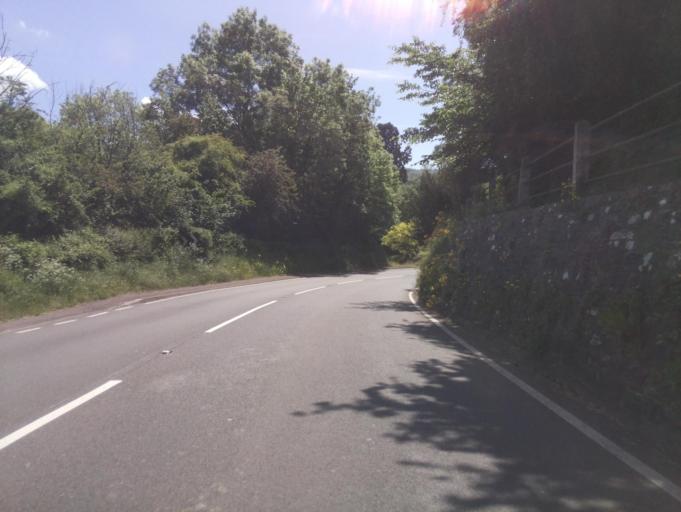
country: GB
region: Wales
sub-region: Monmouthshire
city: Monmouth
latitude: 51.8017
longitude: -2.7136
